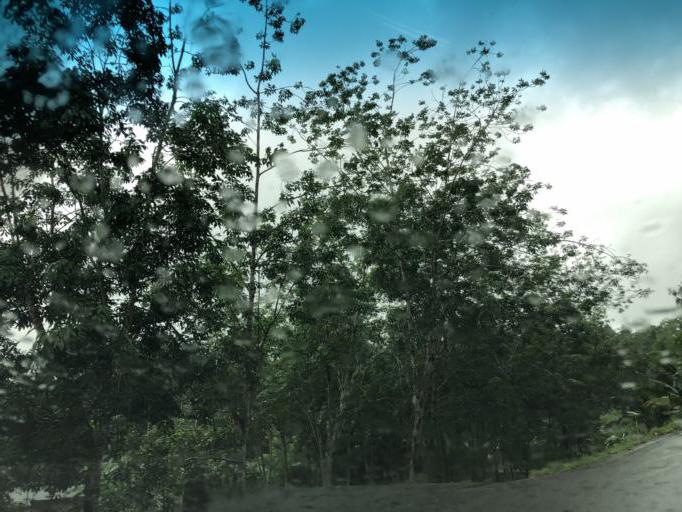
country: LK
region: Western
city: Horana South
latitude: 6.7221
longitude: 80.0614
